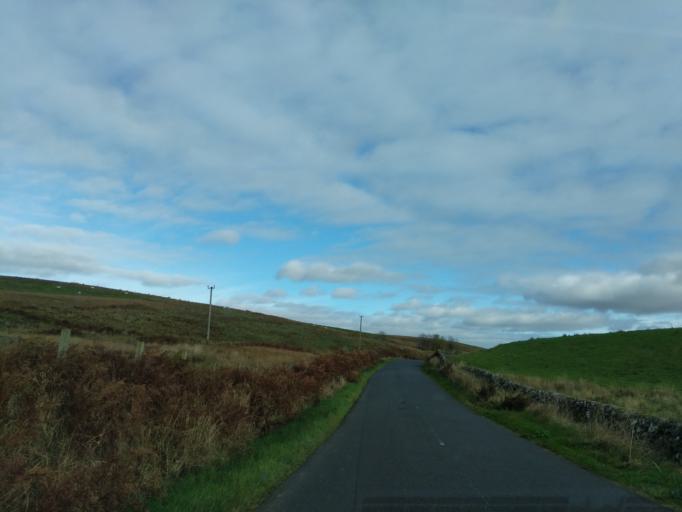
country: GB
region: Scotland
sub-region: Dumfries and Galloway
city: Castle Douglas
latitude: 55.1191
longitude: -4.0876
